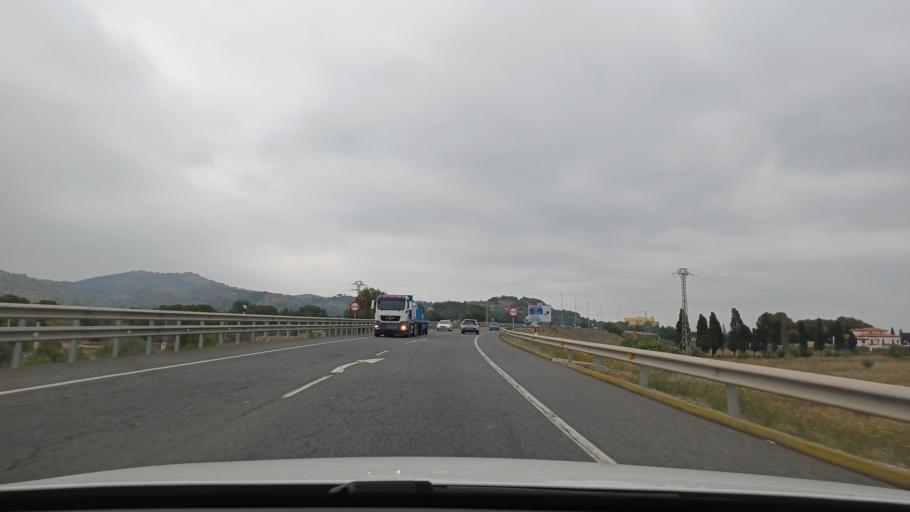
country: ES
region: Valencia
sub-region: Provincia de Castello
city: Borriol
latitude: 40.0012
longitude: -0.0841
